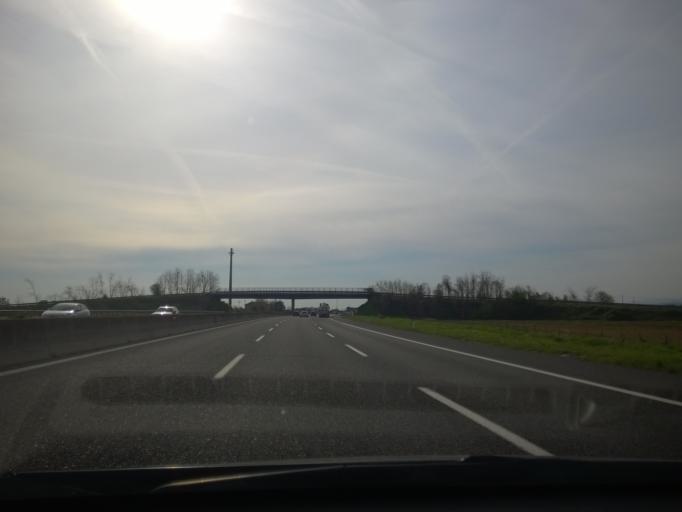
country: IT
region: Emilia-Romagna
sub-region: Forli-Cesena
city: Bagnarola
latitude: 44.1590
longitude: 12.3095
